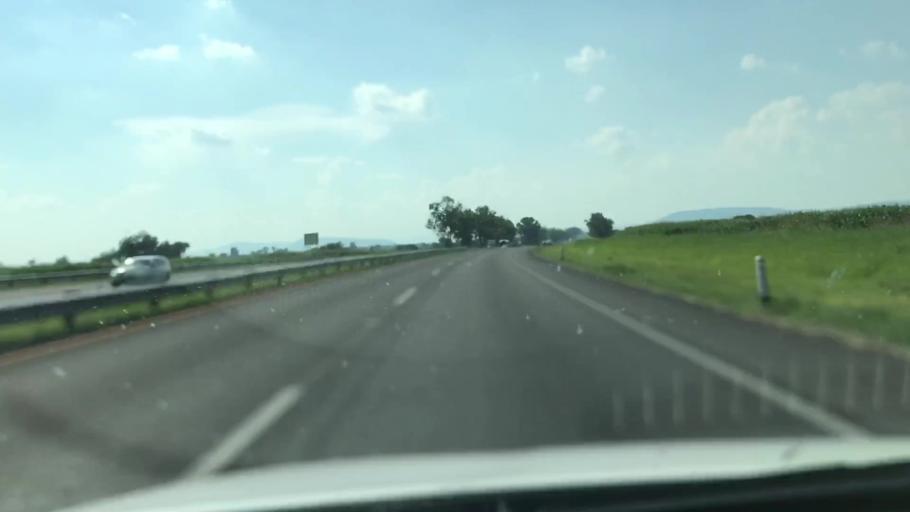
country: MX
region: Jalisco
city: Jamay
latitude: 20.3500
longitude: -102.6319
